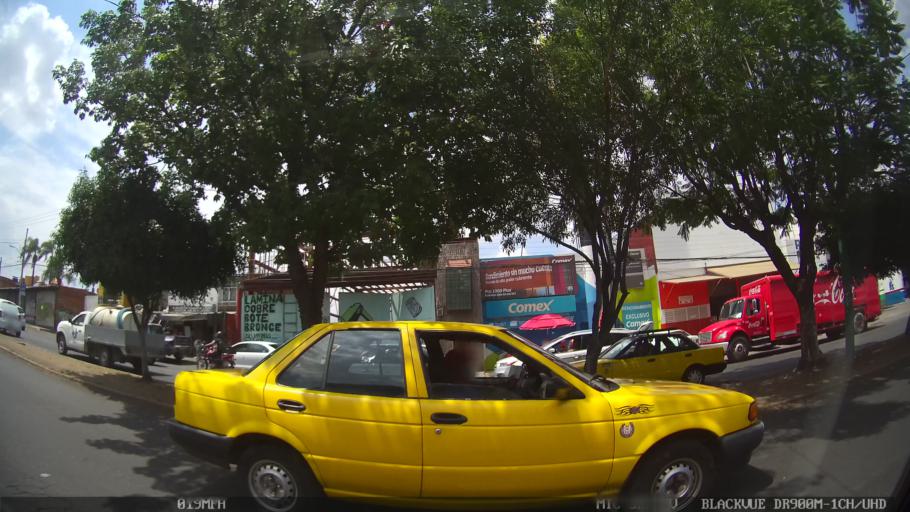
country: MX
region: Jalisco
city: Tlaquepaque
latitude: 20.6321
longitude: -103.2682
